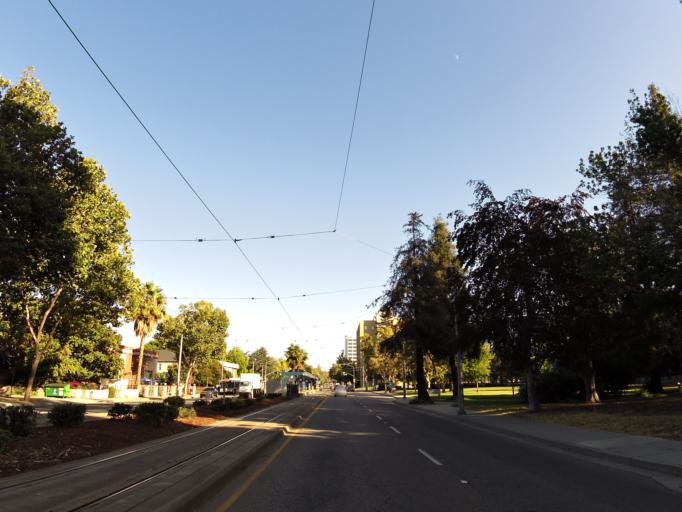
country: US
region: California
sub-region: Santa Clara County
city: San Jose
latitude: 37.3526
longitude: -121.9030
